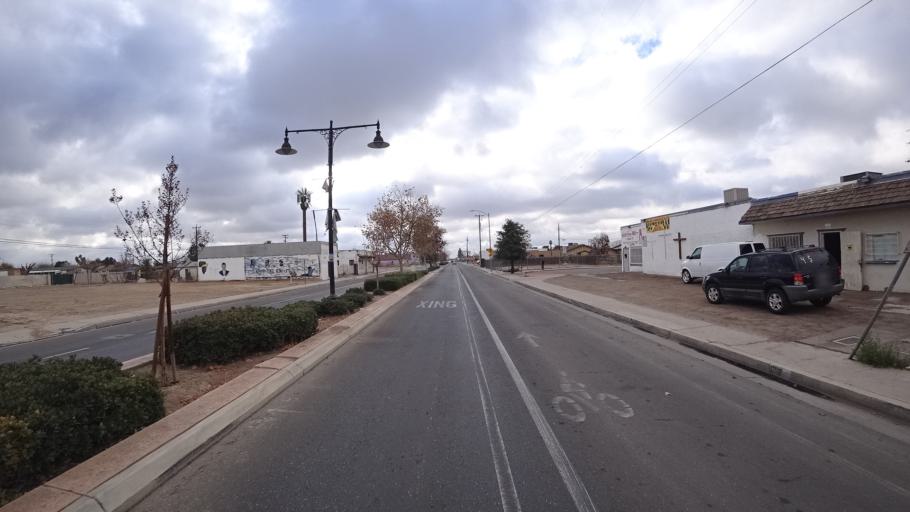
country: US
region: California
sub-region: Kern County
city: Bakersfield
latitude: 35.3634
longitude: -118.9853
